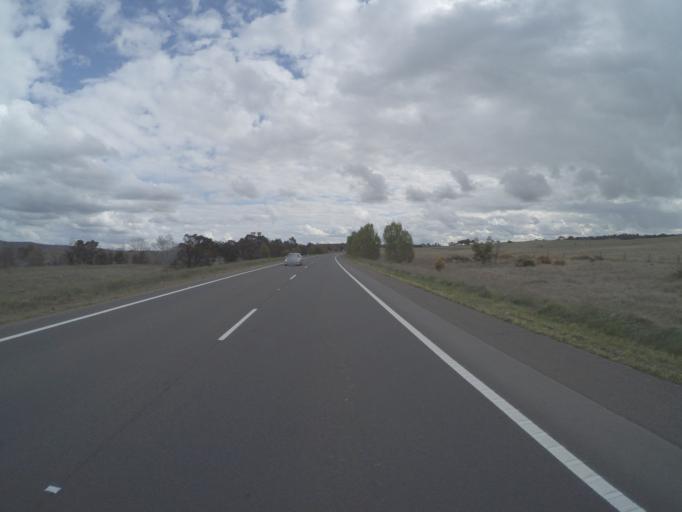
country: AU
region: New South Wales
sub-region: Goulburn Mulwaree
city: Goulburn
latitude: -34.8031
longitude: 149.6082
